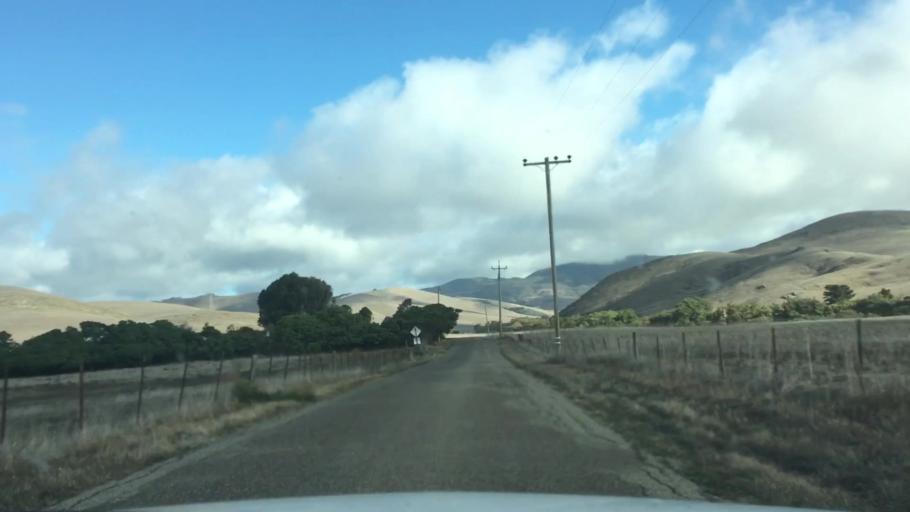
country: US
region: California
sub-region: San Luis Obispo County
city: Morro Bay
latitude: 35.3653
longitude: -120.8059
